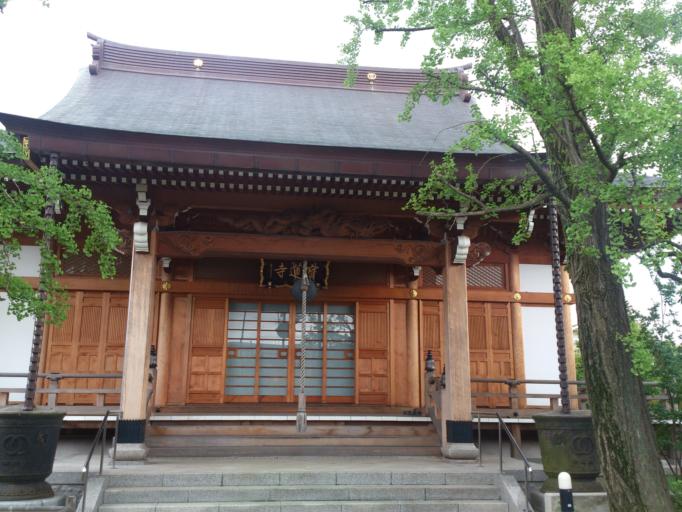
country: JP
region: Chiba
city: Matsudo
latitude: 35.7625
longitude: 139.8573
